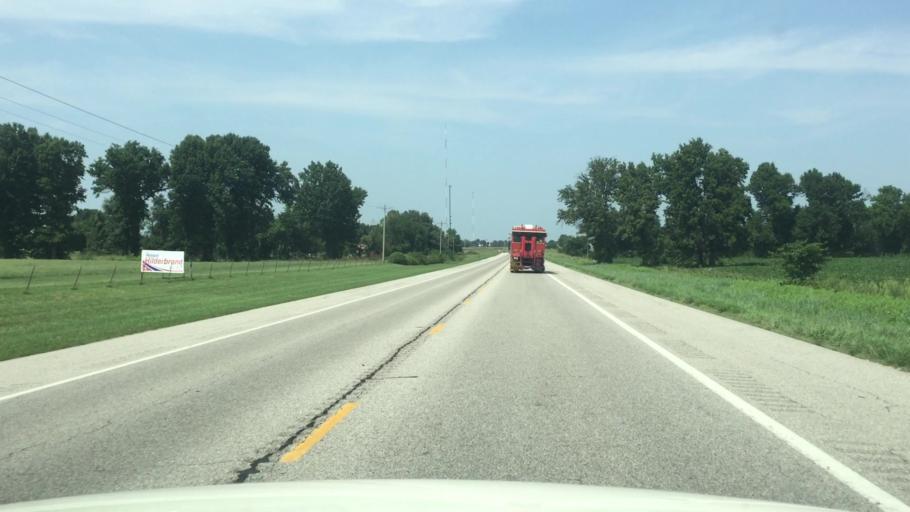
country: US
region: Kansas
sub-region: Cherokee County
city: Galena
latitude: 37.1979
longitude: -94.7047
